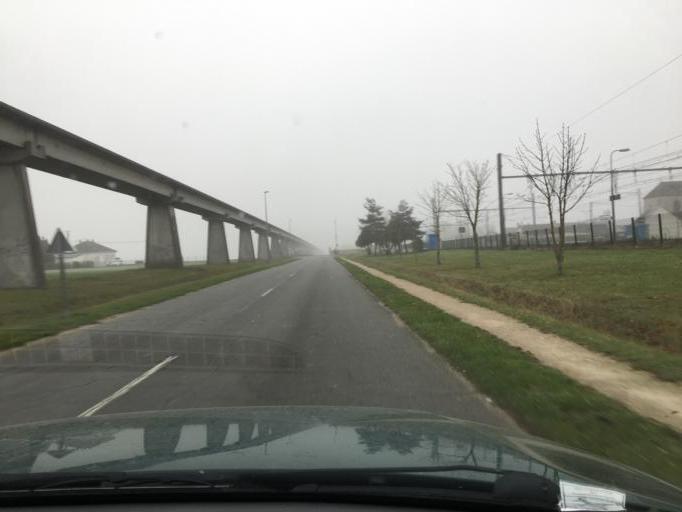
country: FR
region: Centre
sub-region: Departement du Loiret
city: Saran
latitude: 47.9874
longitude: 1.8849
